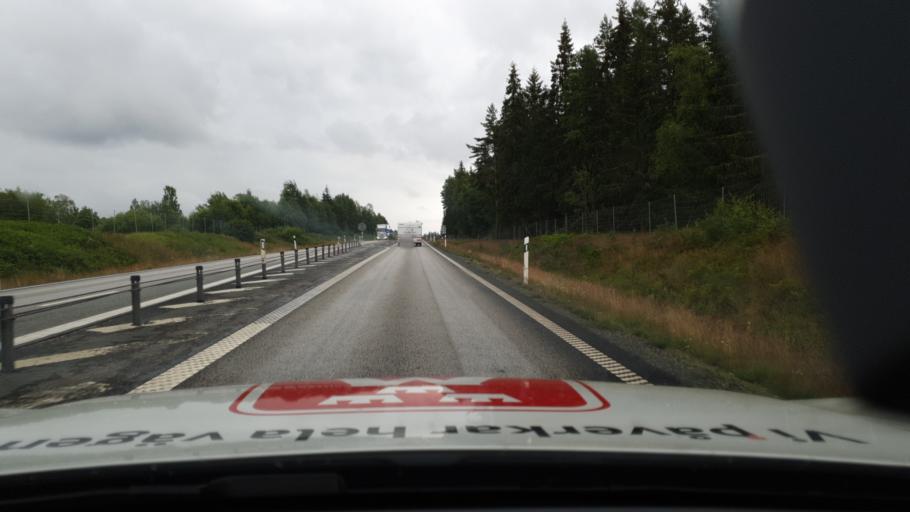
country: SE
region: Joenkoeping
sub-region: Jonkopings Kommun
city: Tenhult
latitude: 57.7058
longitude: 14.4261
